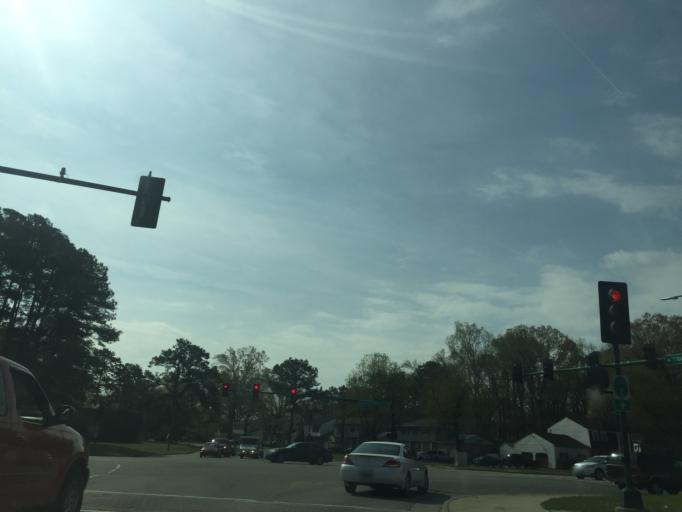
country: US
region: Virginia
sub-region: City of Newport News
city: Newport News
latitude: 37.0640
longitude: -76.4595
